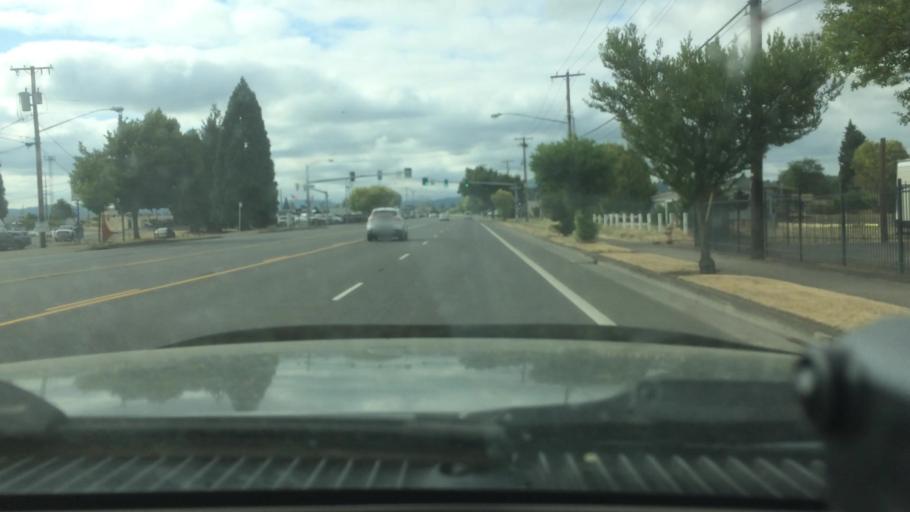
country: US
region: Oregon
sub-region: Lane County
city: Eugene
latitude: 44.0814
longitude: -123.1524
